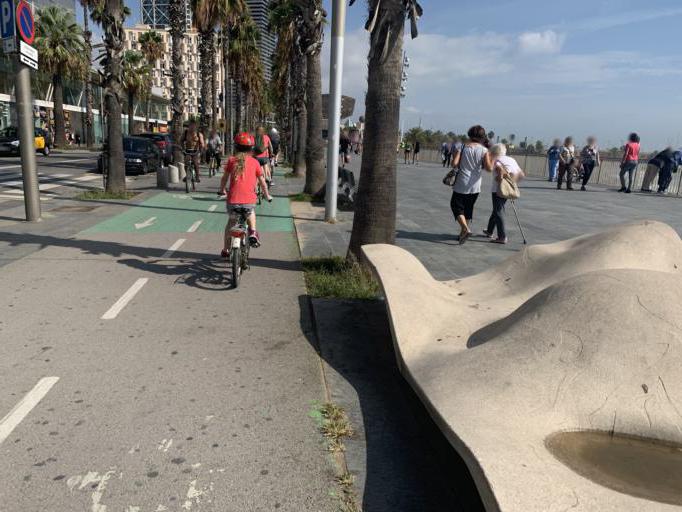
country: ES
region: Catalonia
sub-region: Provincia de Barcelona
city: Ciutat Vella
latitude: 41.3833
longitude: 2.1948
